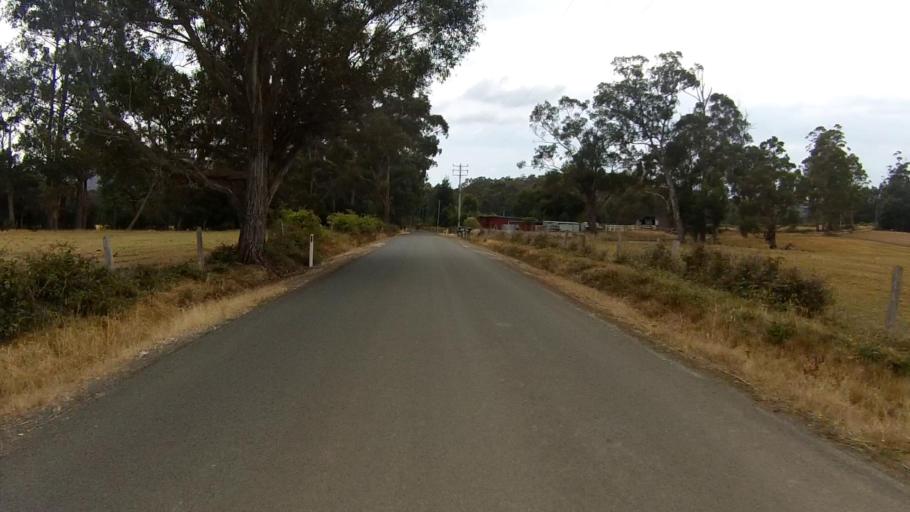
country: AU
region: Tasmania
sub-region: Huon Valley
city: Cygnet
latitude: -43.2387
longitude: 147.1540
